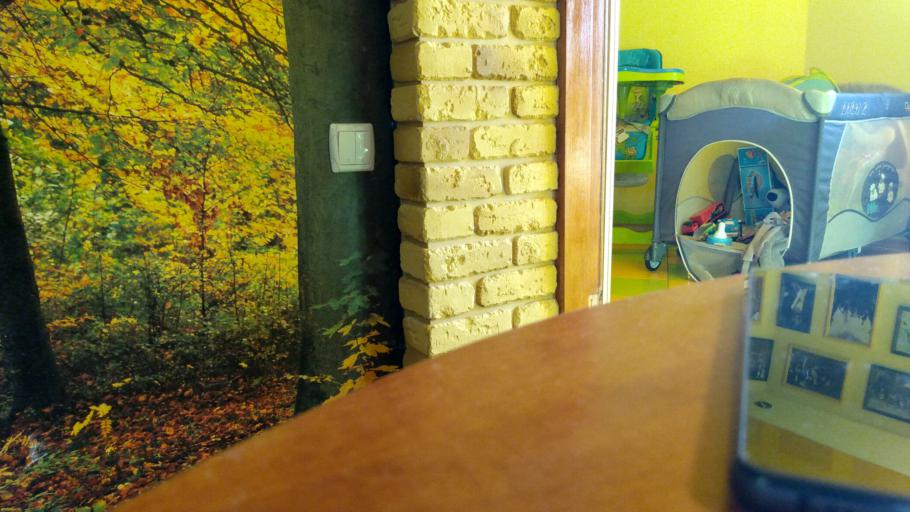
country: RU
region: Tverskaya
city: Likhoslavl'
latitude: 57.1653
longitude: 35.5811
